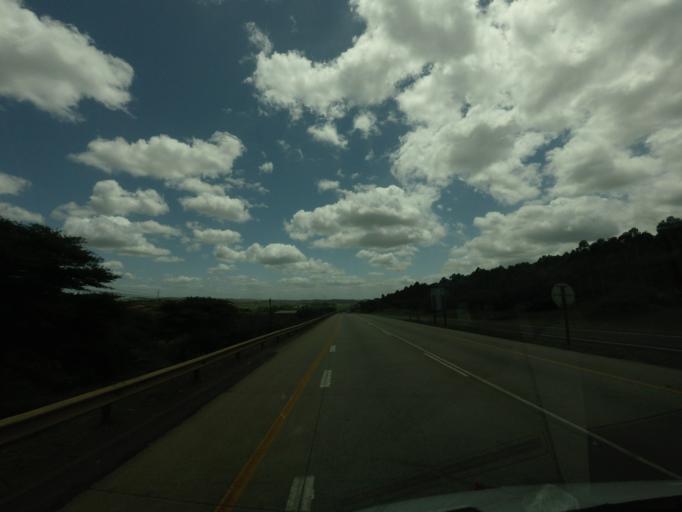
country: ZA
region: KwaZulu-Natal
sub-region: uMkhanyakude District Municipality
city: Mtubatuba
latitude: -28.4672
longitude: 32.1470
